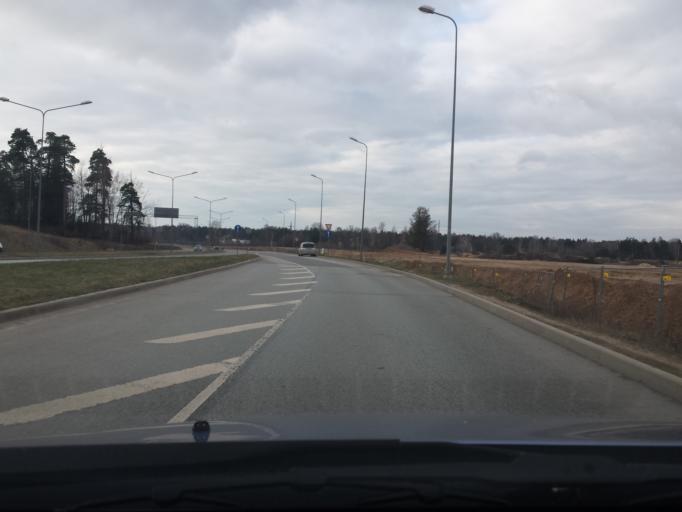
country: LV
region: Riga
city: Jaunciems
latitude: 56.9894
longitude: 24.1590
